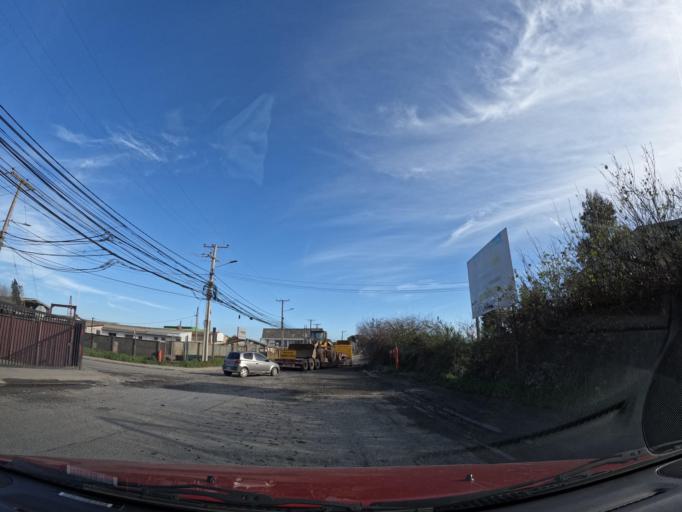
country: CL
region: Biobio
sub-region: Provincia de Concepcion
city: Talcahuano
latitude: -36.7663
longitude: -73.0820
